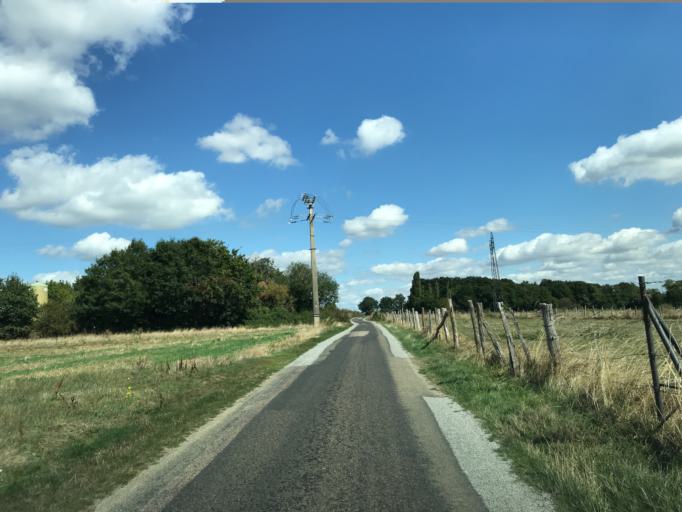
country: FR
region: Haute-Normandie
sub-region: Departement de l'Eure
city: La Chapelle-Reanville
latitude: 49.1195
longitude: 1.3805
